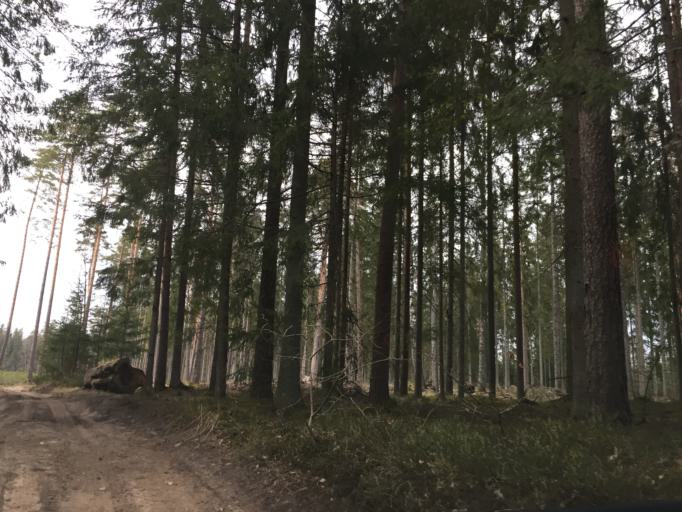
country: LV
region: Sigulda
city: Sigulda
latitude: 57.1313
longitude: 24.8049
